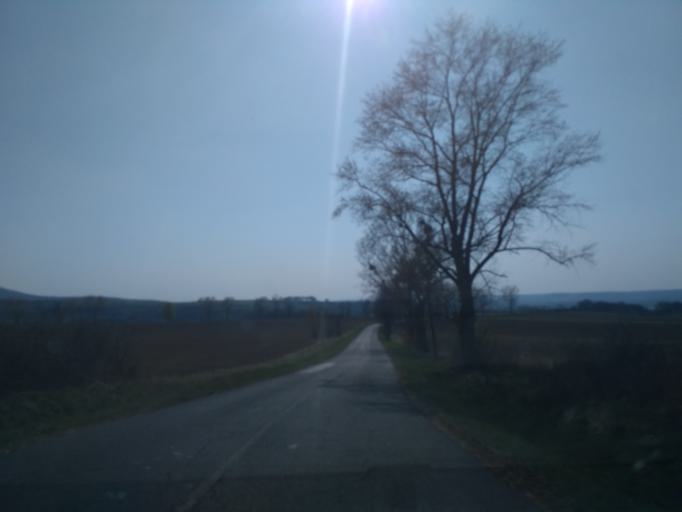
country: HU
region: Borsod-Abauj-Zemplen
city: Gonc
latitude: 48.5357
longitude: 21.3361
